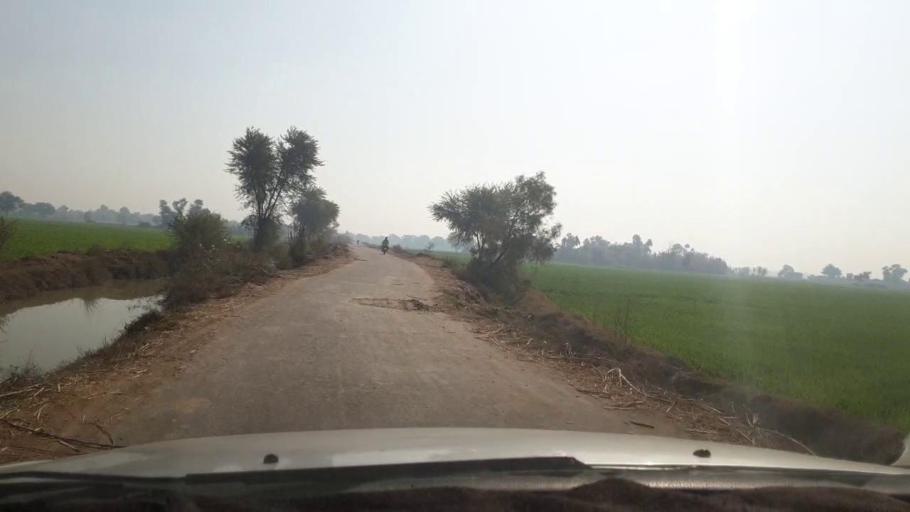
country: PK
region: Sindh
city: Khanpur
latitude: 27.7344
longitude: 69.5113
